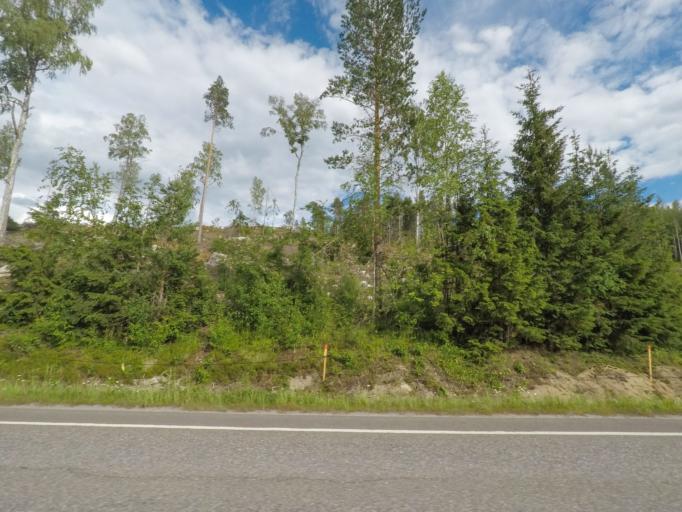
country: FI
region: Uusimaa
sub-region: Porvoo
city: Pukkila
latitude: 60.7983
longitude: 25.4712
